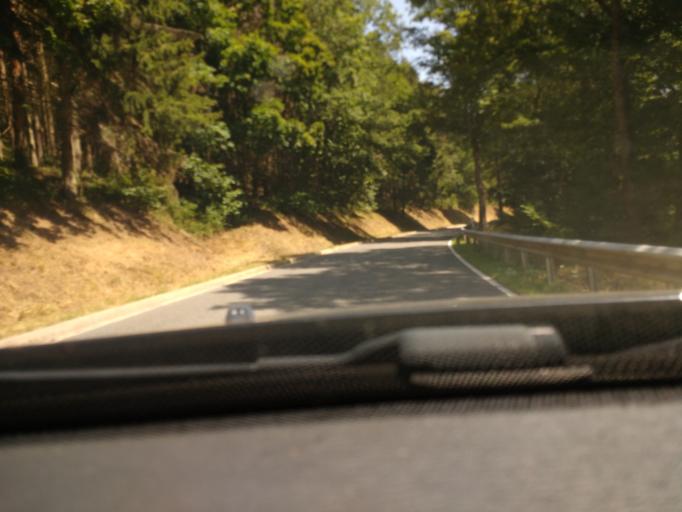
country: DE
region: Rheinland-Pfalz
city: Bettenfeld
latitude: 50.0898
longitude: 6.7835
